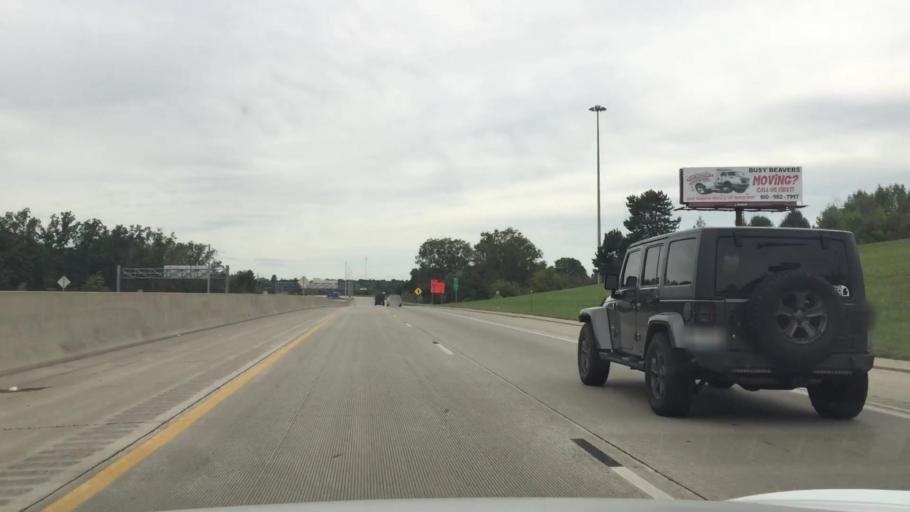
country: US
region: Michigan
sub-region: Saint Clair County
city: Port Huron
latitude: 42.9893
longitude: -82.4588
